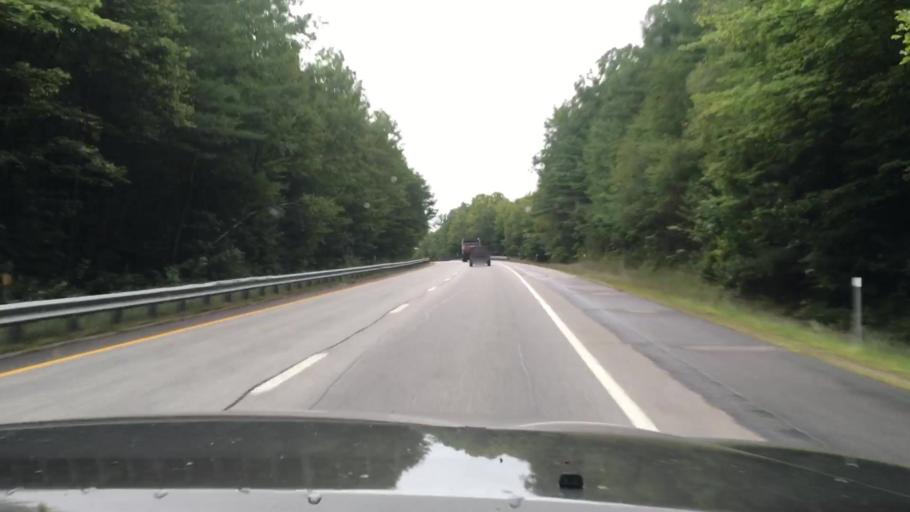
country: US
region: New Hampshire
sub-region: Belknap County
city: Sanbornton
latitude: 43.4825
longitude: -71.5923
